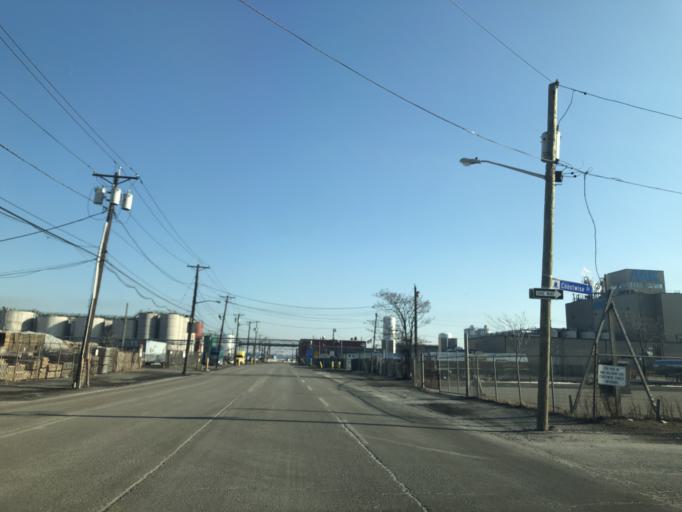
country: US
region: New Jersey
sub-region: Hudson County
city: Bayonne
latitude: 40.6935
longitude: -74.1463
